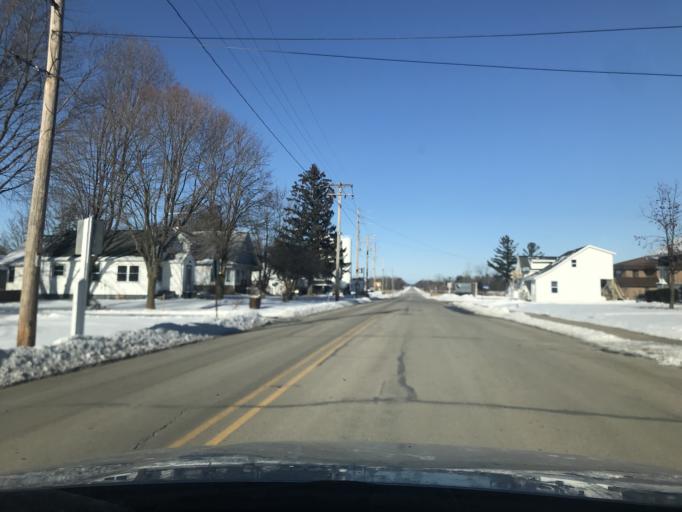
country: US
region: Wisconsin
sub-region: Oconto County
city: Oconto Falls
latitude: 44.9526
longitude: -88.0468
